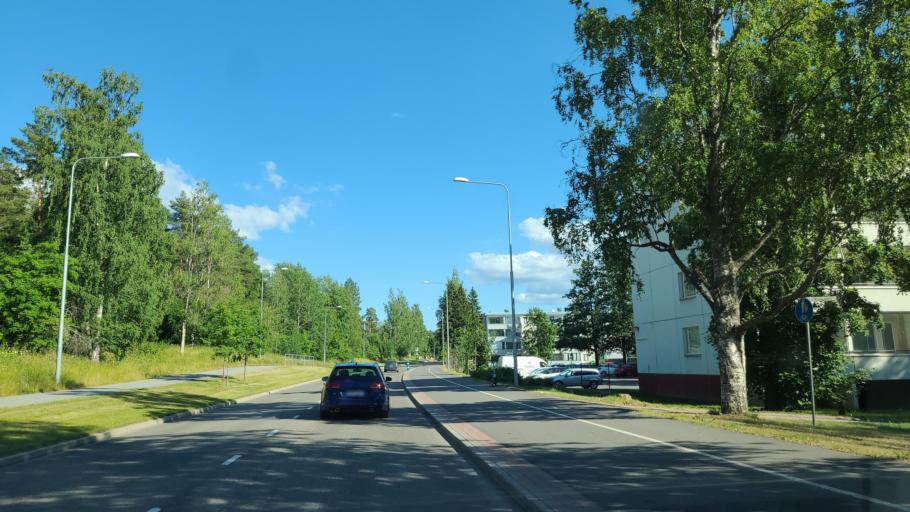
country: FI
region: Central Finland
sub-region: Jyvaeskylae
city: Jyvaeskylae
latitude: 62.2471
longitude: 25.7825
